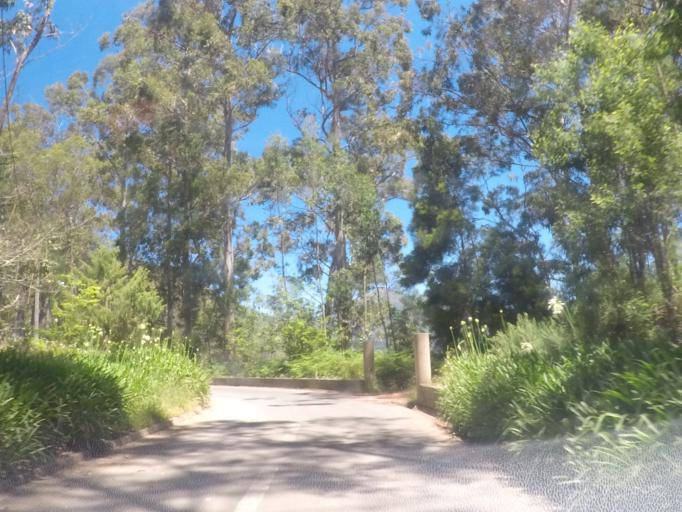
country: PT
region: Madeira
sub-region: Camara de Lobos
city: Curral das Freiras
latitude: 32.6951
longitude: -16.9779
